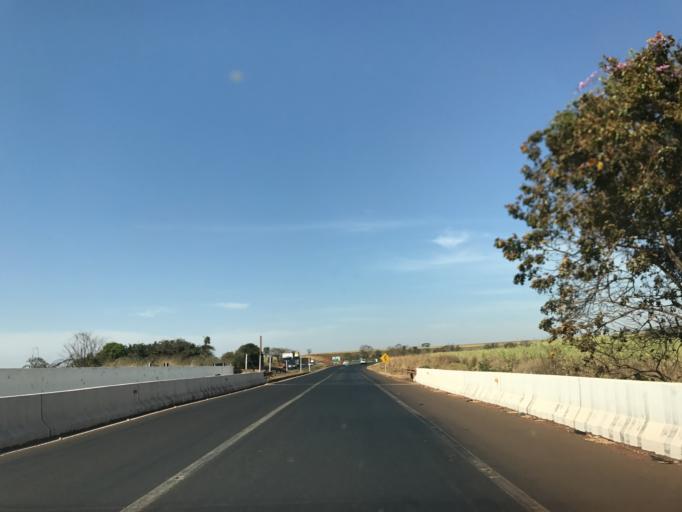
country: BR
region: Minas Gerais
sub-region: Centralina
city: Centralina
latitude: -18.5384
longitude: -49.1932
